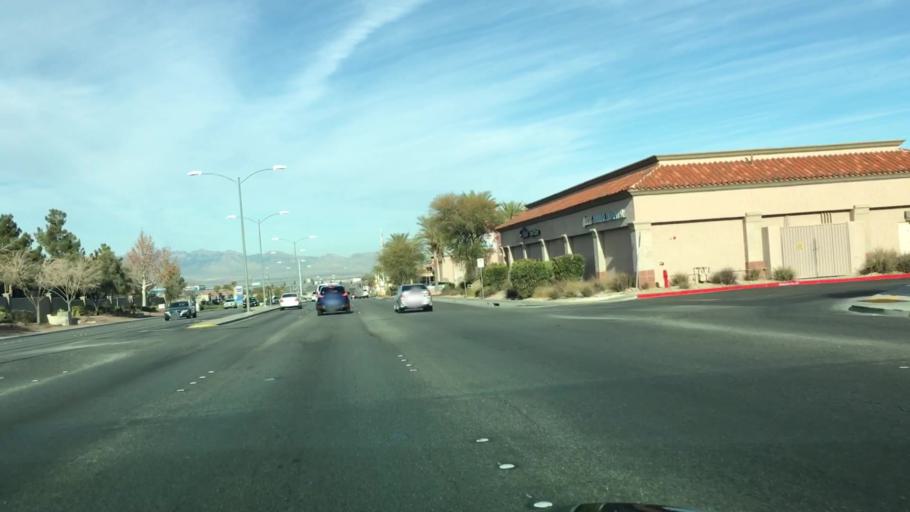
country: US
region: Nevada
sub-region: Clark County
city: Whitney
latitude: 35.9973
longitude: -115.1023
